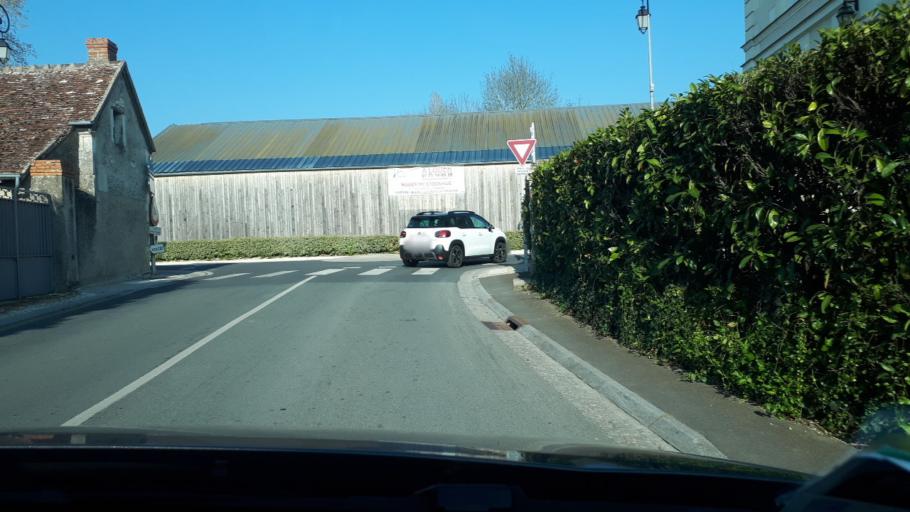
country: FR
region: Centre
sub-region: Departement d'Indre-et-Loire
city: La Croix-en-Touraine
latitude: 47.3356
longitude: 0.9902
